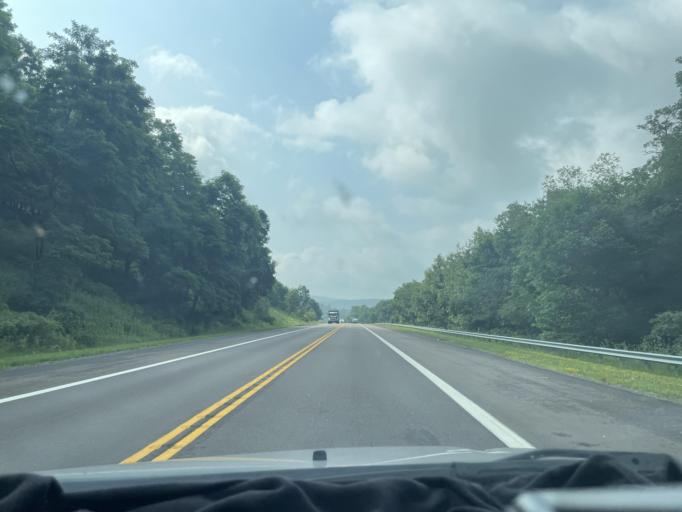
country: US
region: Maryland
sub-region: Garrett County
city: Oakland
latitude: 39.5435
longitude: -79.3504
